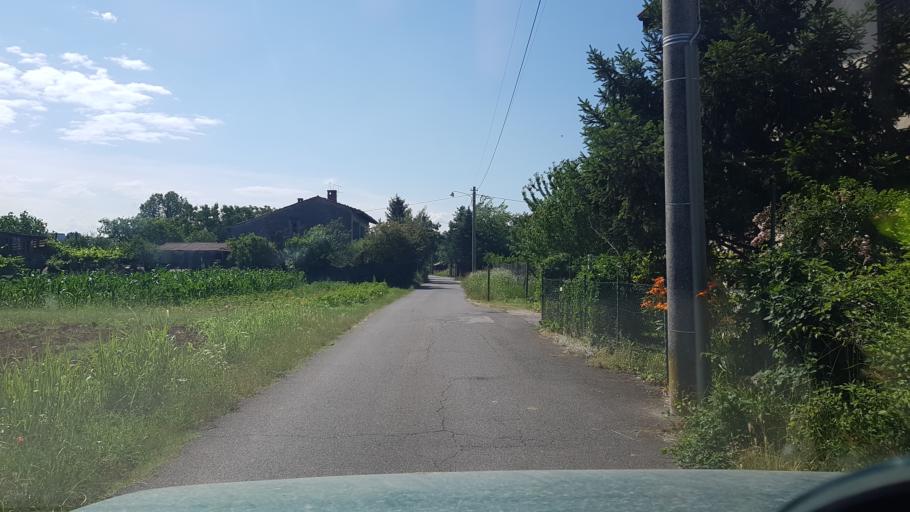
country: SI
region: Nova Gorica
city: Nova Gorica
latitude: 45.9630
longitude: 13.6294
